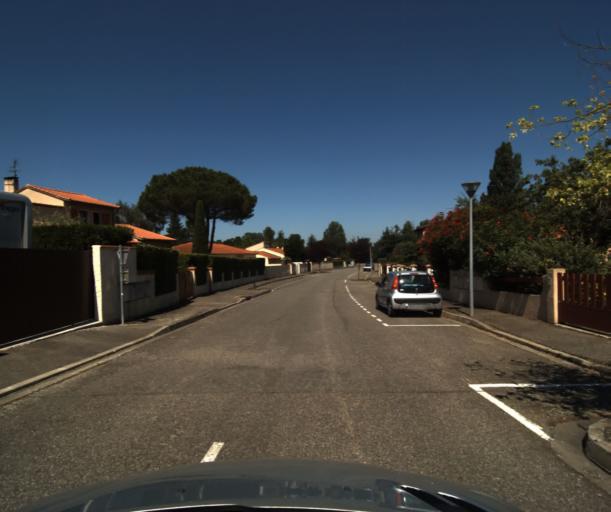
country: FR
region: Midi-Pyrenees
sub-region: Departement de la Haute-Garonne
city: Roquettes
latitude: 43.4978
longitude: 1.3752
